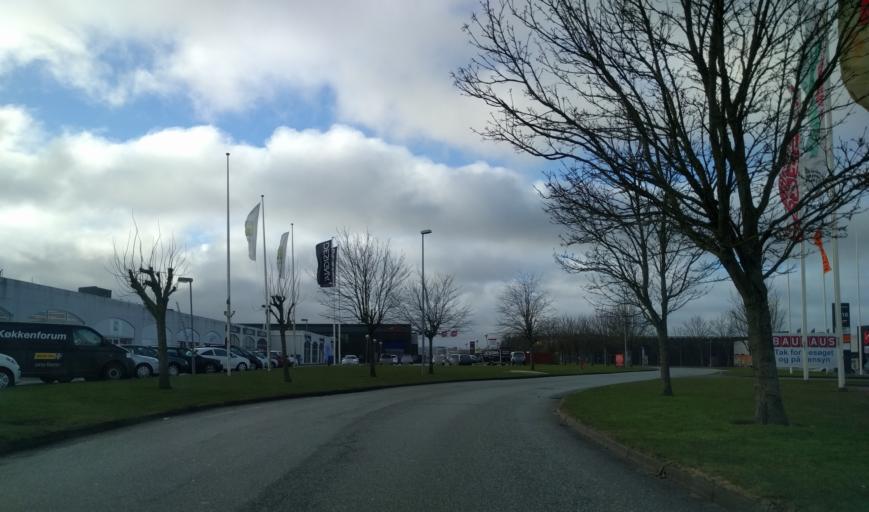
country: DK
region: North Denmark
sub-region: Alborg Kommune
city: Svenstrup
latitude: 56.9995
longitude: 9.8728
